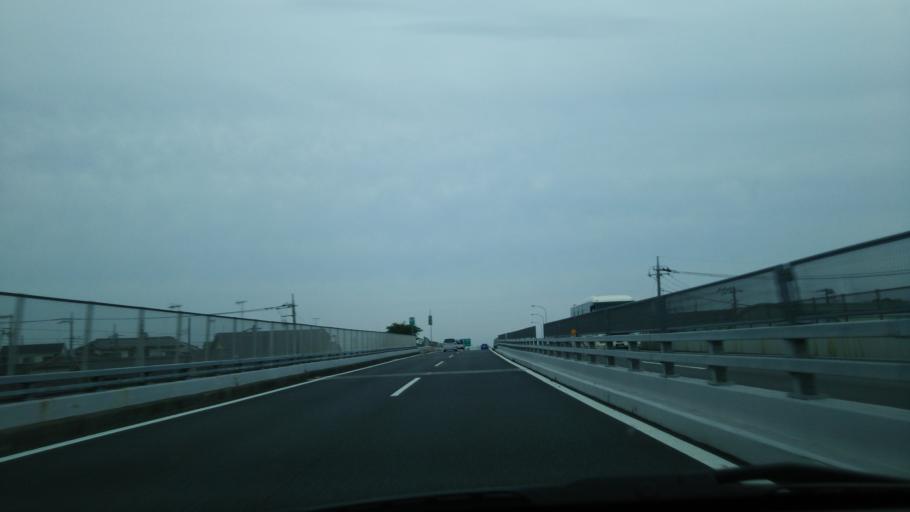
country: JP
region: Kanagawa
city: Isehara
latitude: 35.3567
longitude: 139.3012
